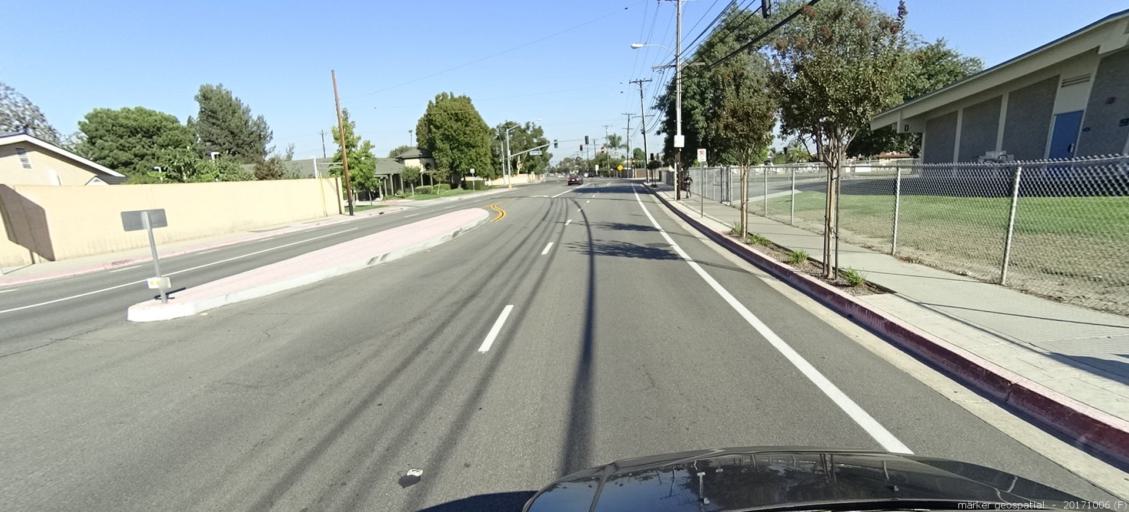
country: US
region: California
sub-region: Orange County
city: Westminster
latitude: 33.7811
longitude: -118.0212
